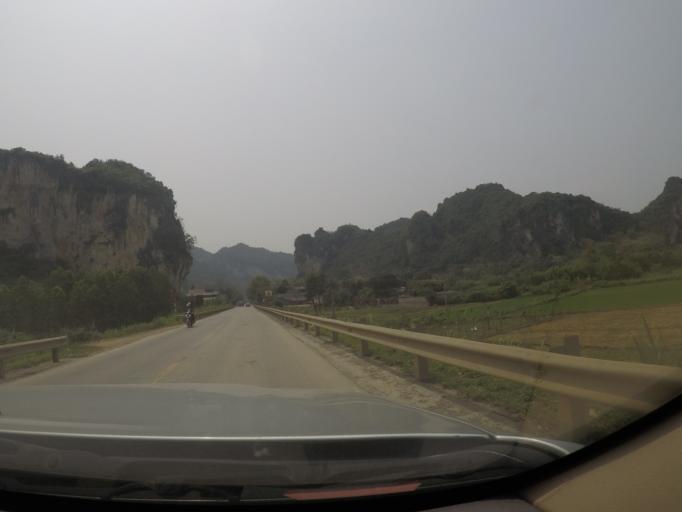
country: VN
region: Thanh Hoa
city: Thi Tran Cam Thuy
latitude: 20.2268
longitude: 105.4927
